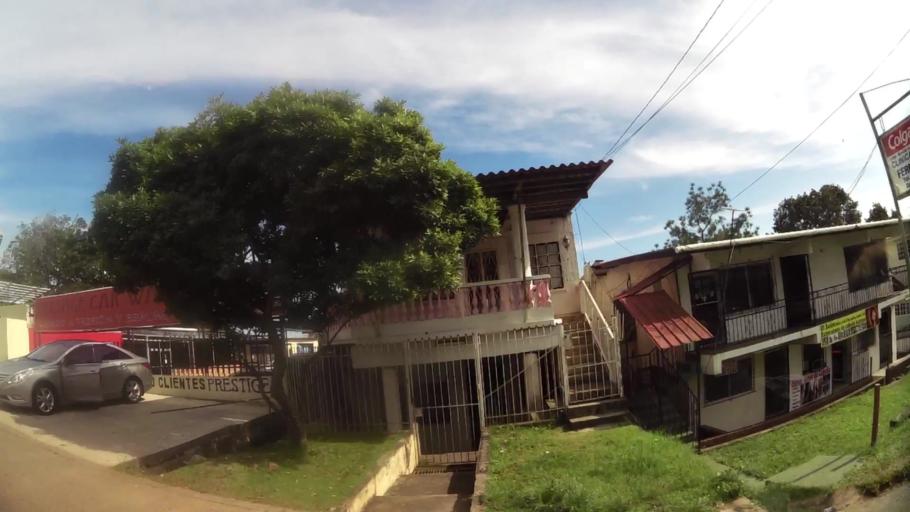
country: PA
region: Panama
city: La Chorrera
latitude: 8.8822
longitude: -79.7787
